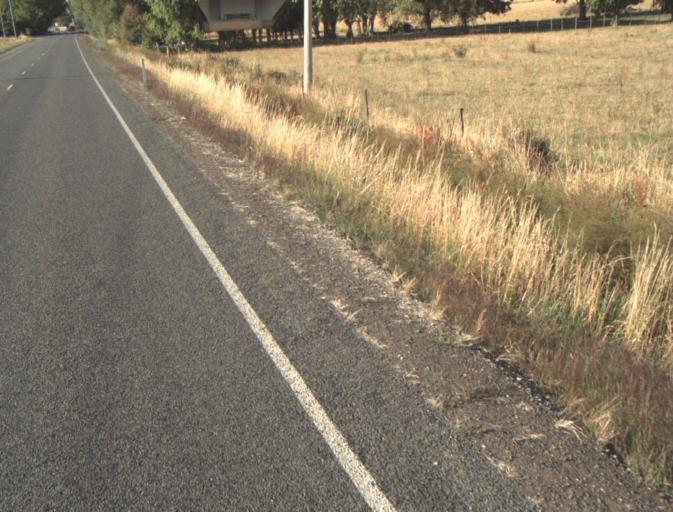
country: AU
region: Tasmania
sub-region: Launceston
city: Mayfield
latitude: -41.2458
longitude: 147.2173
